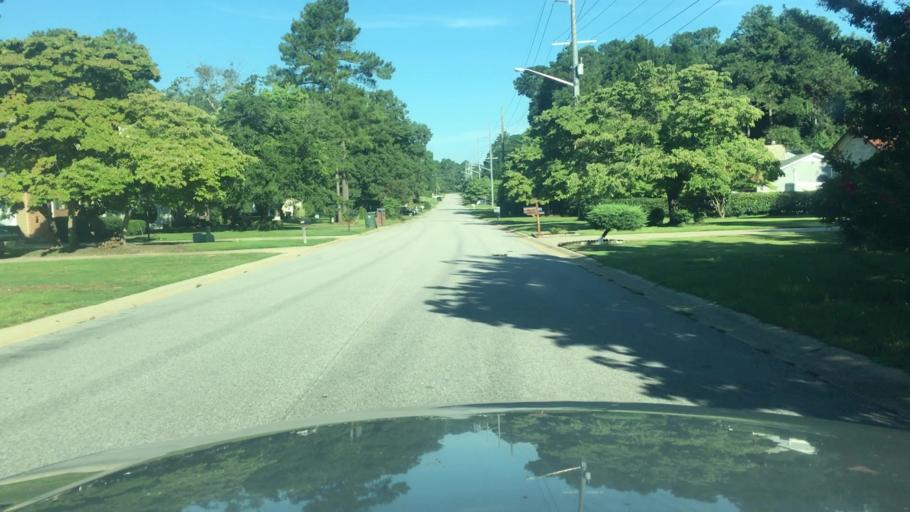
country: US
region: North Carolina
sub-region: Cumberland County
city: Fayetteville
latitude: 35.1299
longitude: -78.8860
